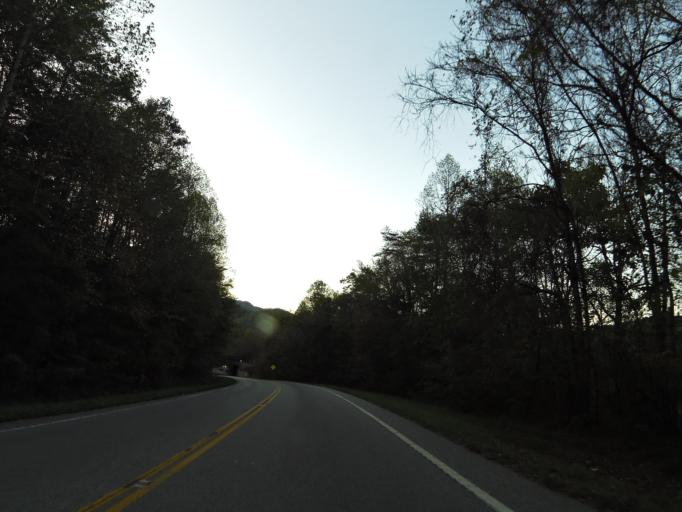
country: US
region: Tennessee
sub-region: Campbell County
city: Caryville
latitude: 36.2713
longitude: -84.1964
